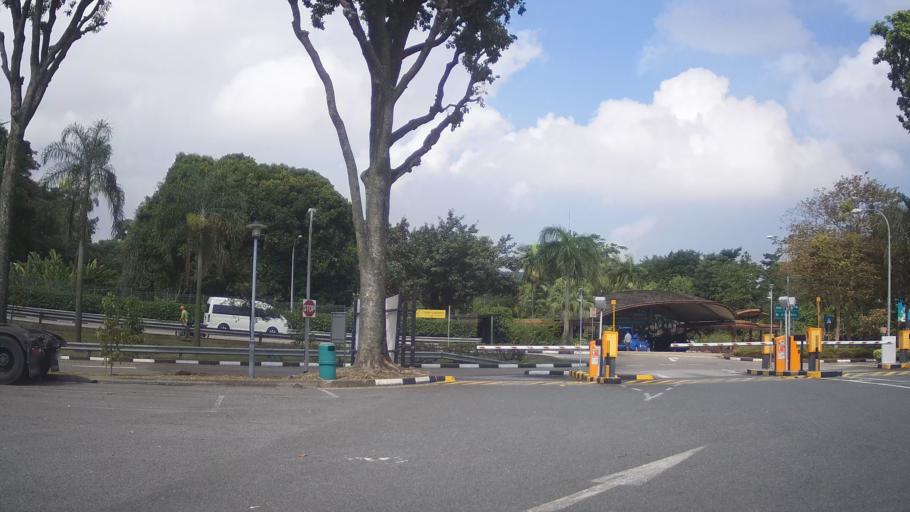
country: SG
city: Singapore
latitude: 1.3208
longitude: 103.7077
